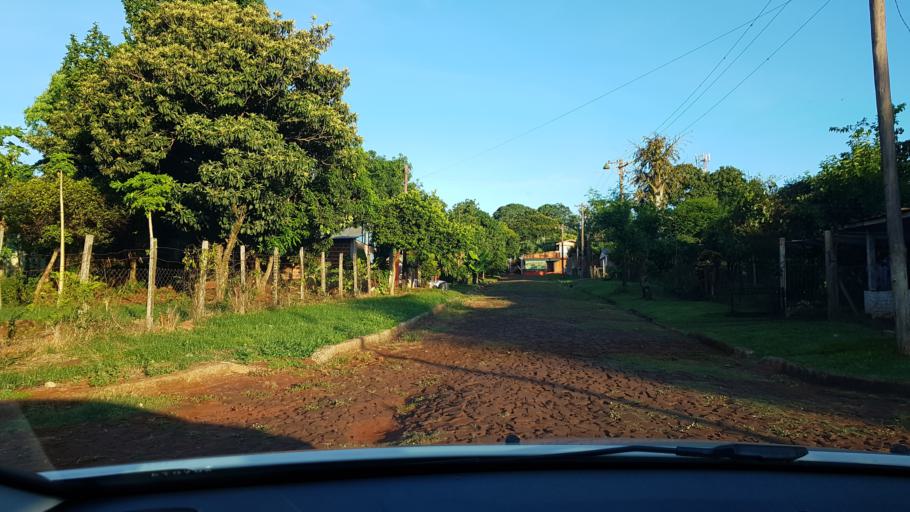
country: AR
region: Misiones
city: Puerto Libertad
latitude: -25.9164
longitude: -54.5814
